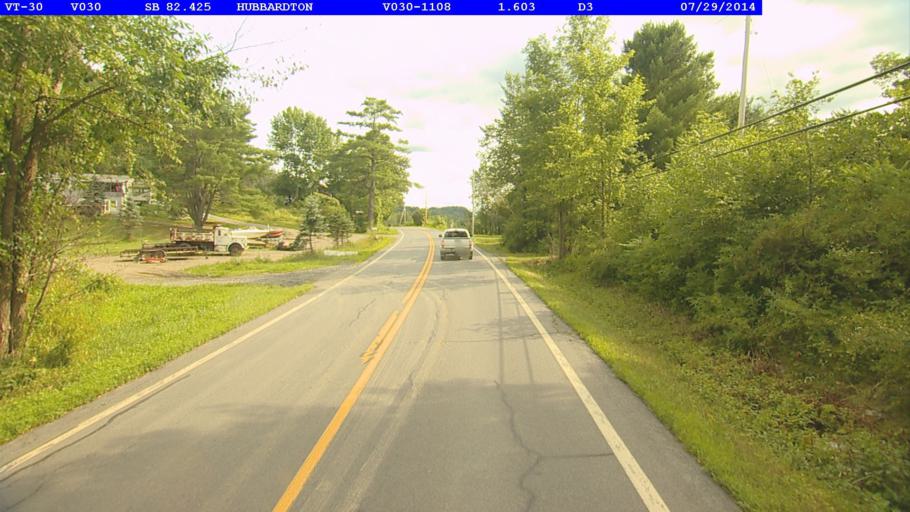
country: US
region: Vermont
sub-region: Rutland County
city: Castleton
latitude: 43.7010
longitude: -73.1855
